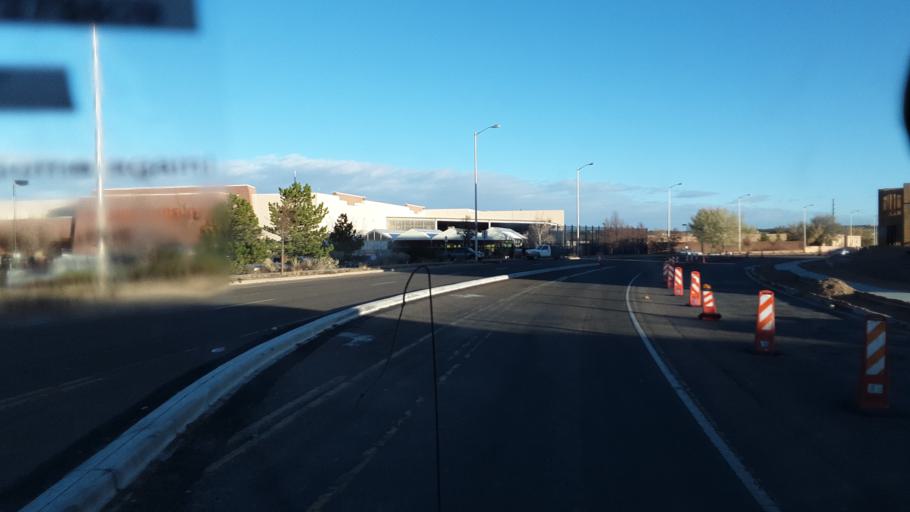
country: US
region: New Mexico
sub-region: Santa Fe County
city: Agua Fria
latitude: 35.6511
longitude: -106.0020
